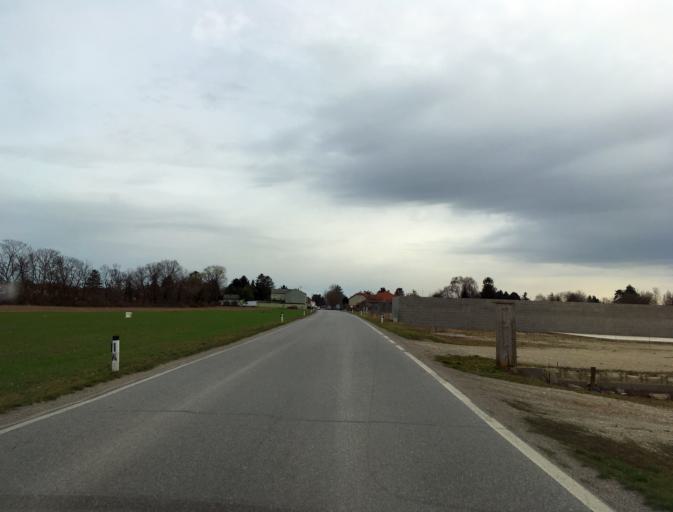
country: AT
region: Lower Austria
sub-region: Politischer Bezirk Ganserndorf
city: Leopoldsdorf im Marchfelde
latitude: 48.2275
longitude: 16.6828
